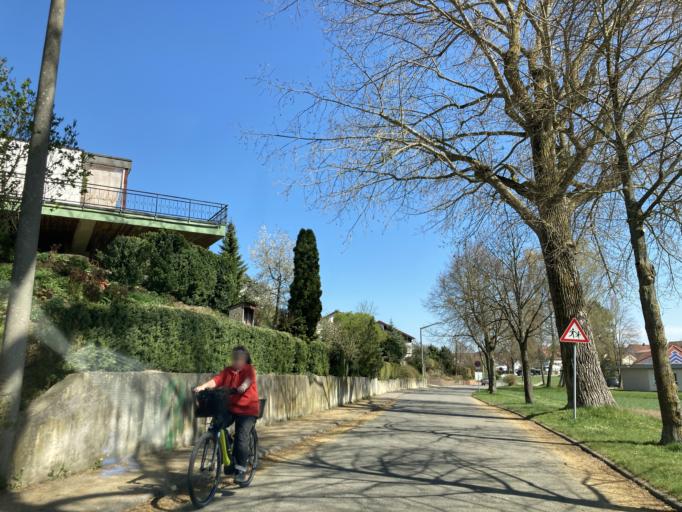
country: DE
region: Baden-Wuerttemberg
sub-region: Regierungsbezirk Stuttgart
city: Bondorf
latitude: 48.5299
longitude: 8.8628
